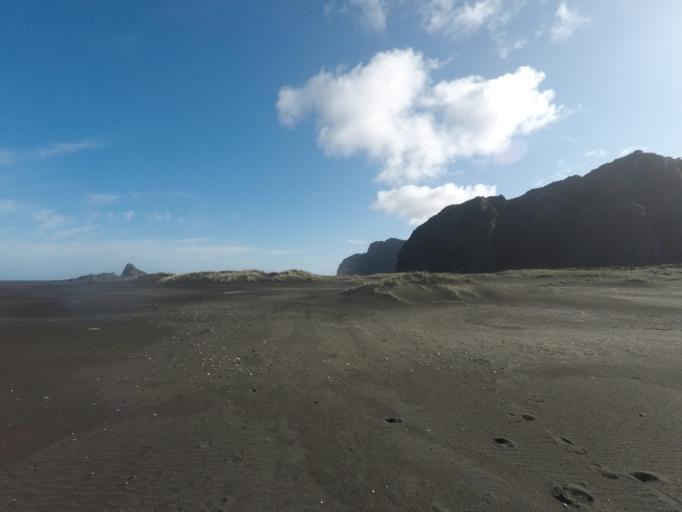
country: NZ
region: Auckland
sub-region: Auckland
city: Muriwai Beach
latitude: -36.9971
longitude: 174.4747
